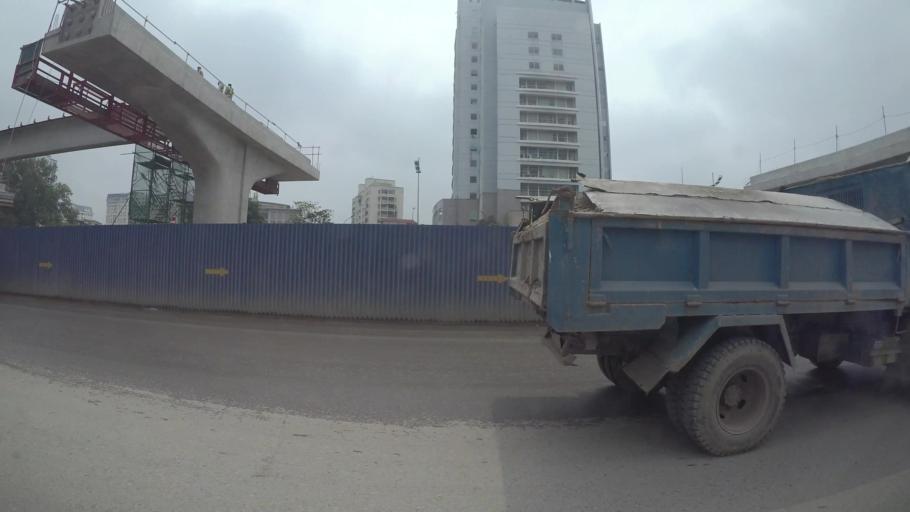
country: VN
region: Ha Noi
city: Cau Dien
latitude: 21.0476
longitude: 105.7812
